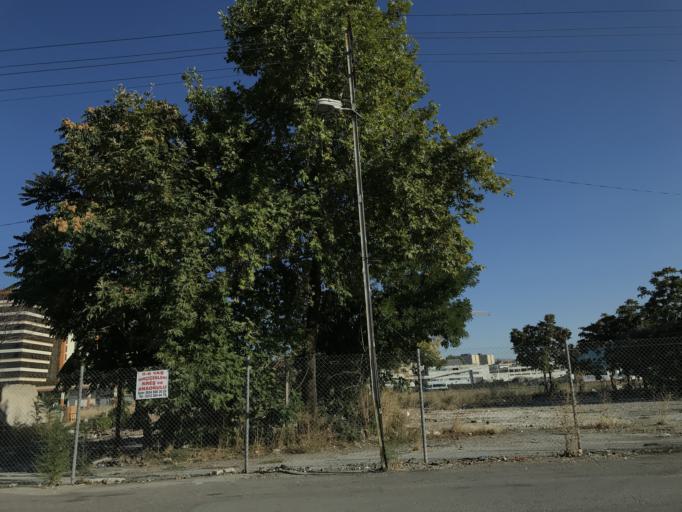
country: TR
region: Ankara
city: Ankara
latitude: 39.9504
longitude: 32.8464
